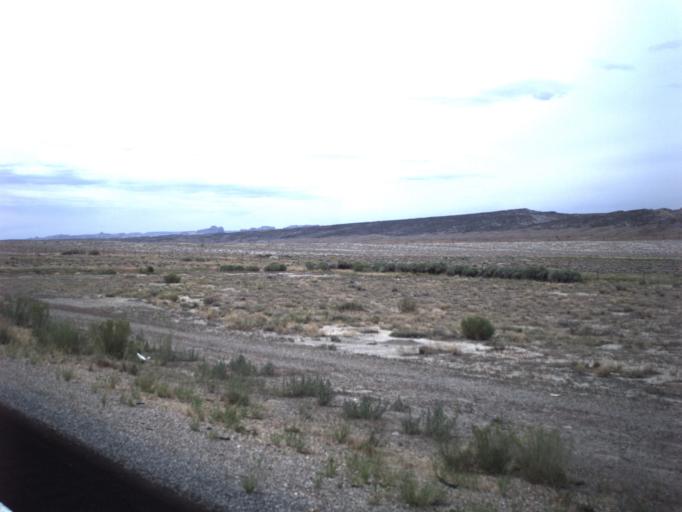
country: US
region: Utah
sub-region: Carbon County
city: East Carbon City
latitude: 39.1923
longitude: -110.3385
